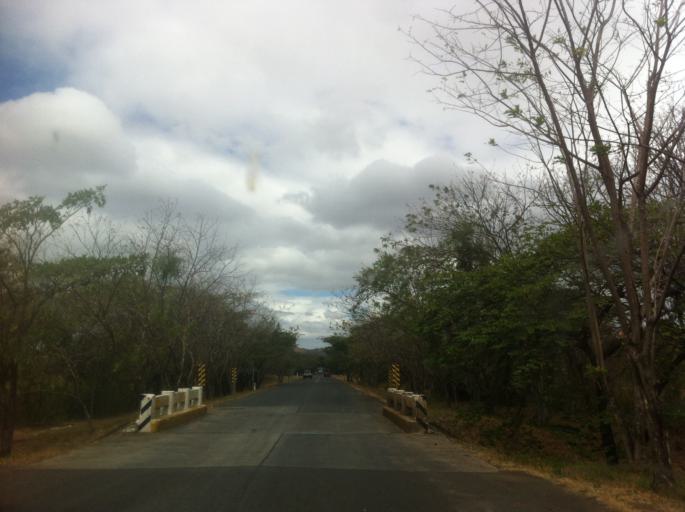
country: NI
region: Chontales
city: Juigalpa
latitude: 12.0620
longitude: -85.3015
